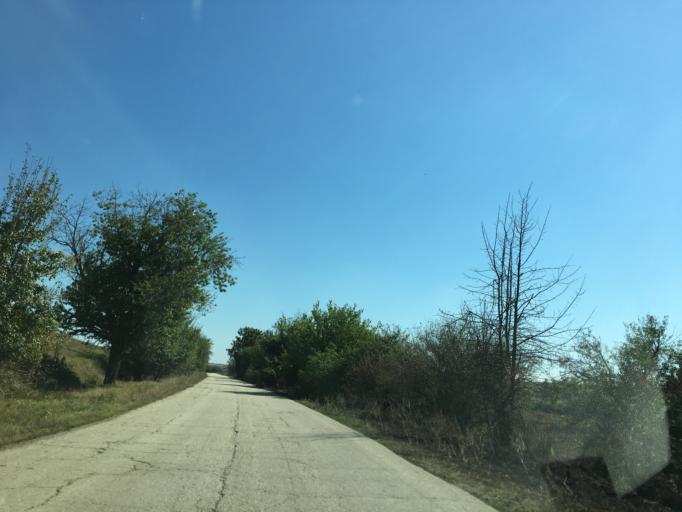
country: BG
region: Pleven
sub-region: Obshtina Knezha
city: Knezha
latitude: 43.5386
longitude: 24.1108
